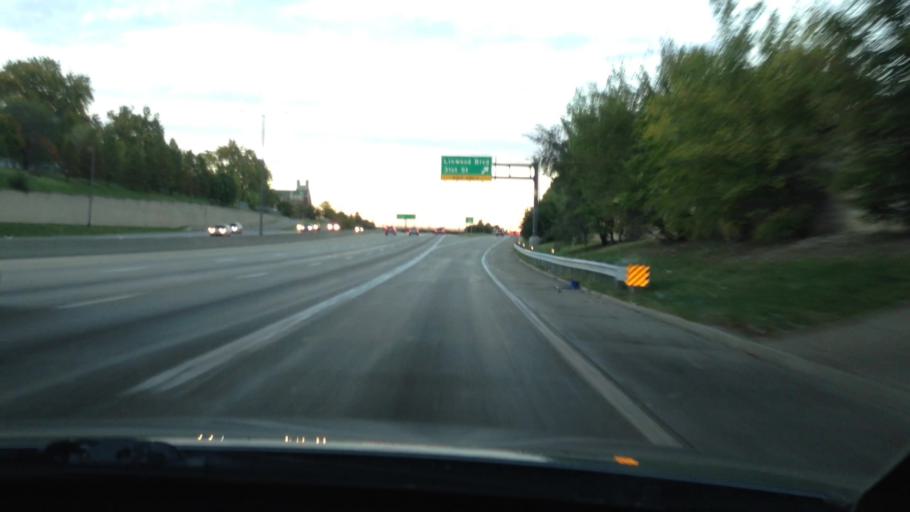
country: US
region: Missouri
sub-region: Jackson County
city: Kansas City
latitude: 39.0629
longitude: -94.5605
